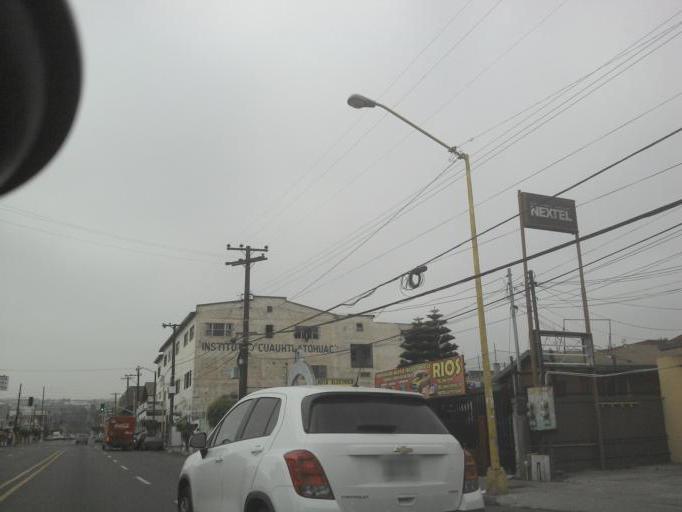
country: MX
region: Baja California
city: Tijuana
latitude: 32.5269
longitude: -117.0312
